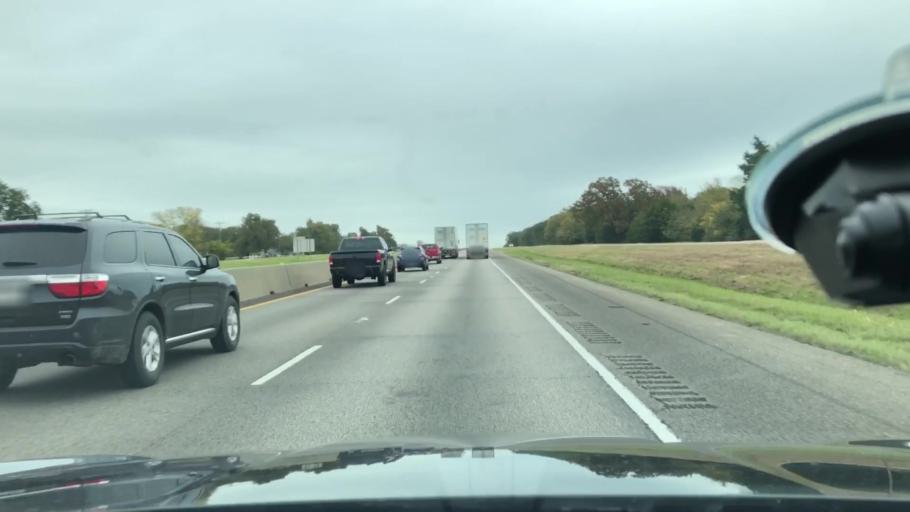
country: US
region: Texas
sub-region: Hopkins County
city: Sulphur Springs
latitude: 33.1465
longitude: -95.5474
